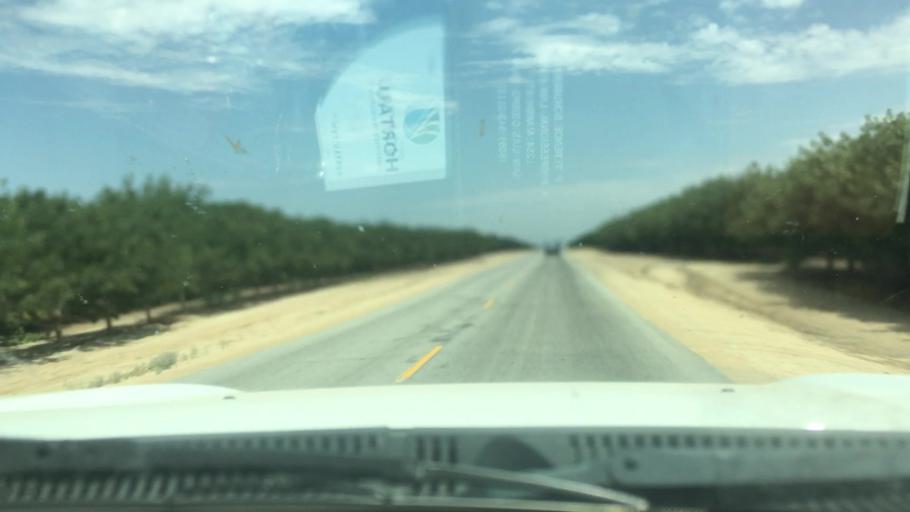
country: US
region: California
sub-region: Kern County
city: McFarland
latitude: 35.5822
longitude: -119.1511
